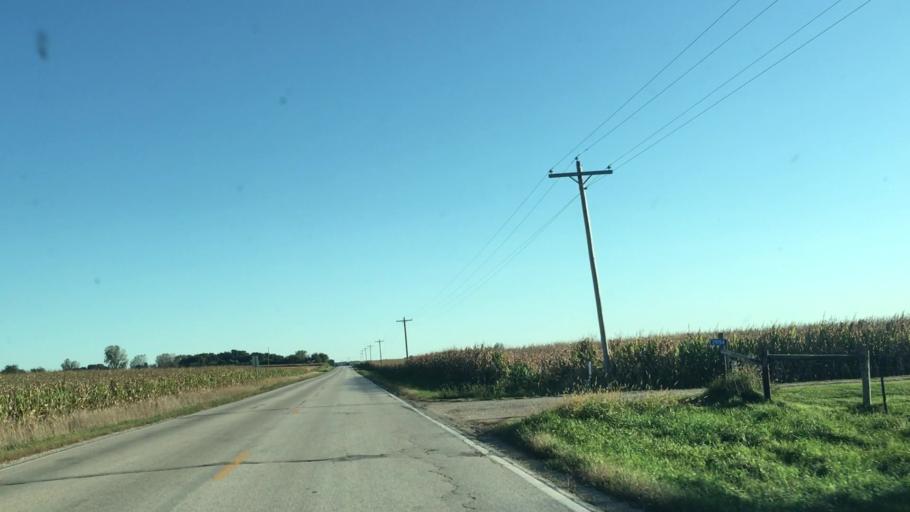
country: US
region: Minnesota
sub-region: Fillmore County
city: Chatfield
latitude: 43.8315
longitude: -92.0694
